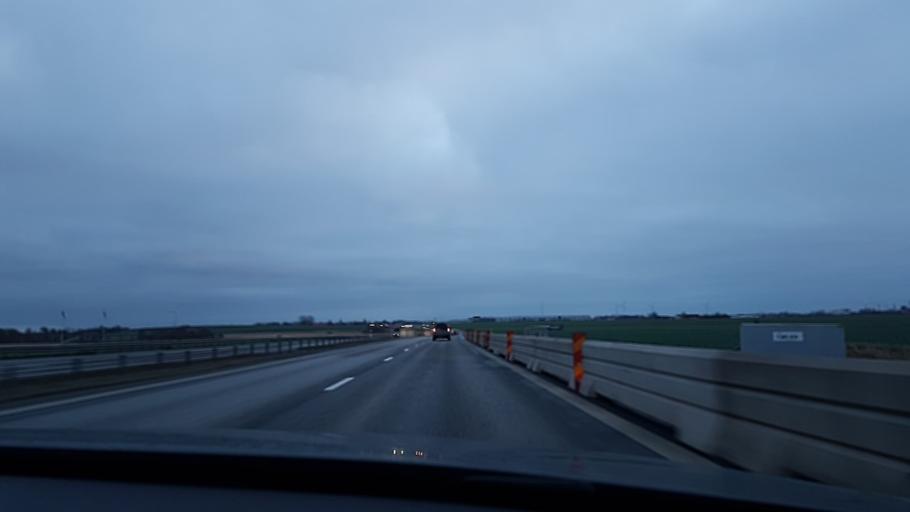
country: SE
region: Skane
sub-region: Landskrona
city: Landskrona
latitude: 55.8990
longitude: 12.8665
